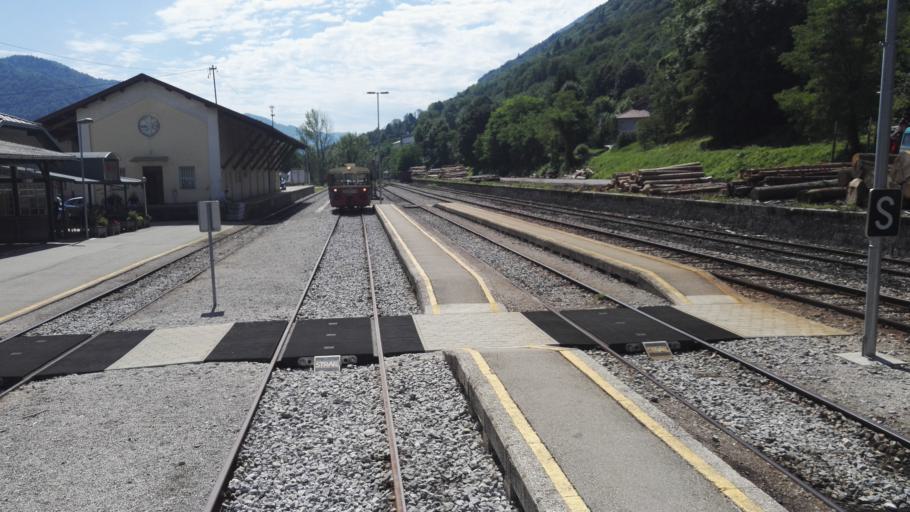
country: SI
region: Tolmin
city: Tolmin
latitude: 46.1465
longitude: 13.7593
